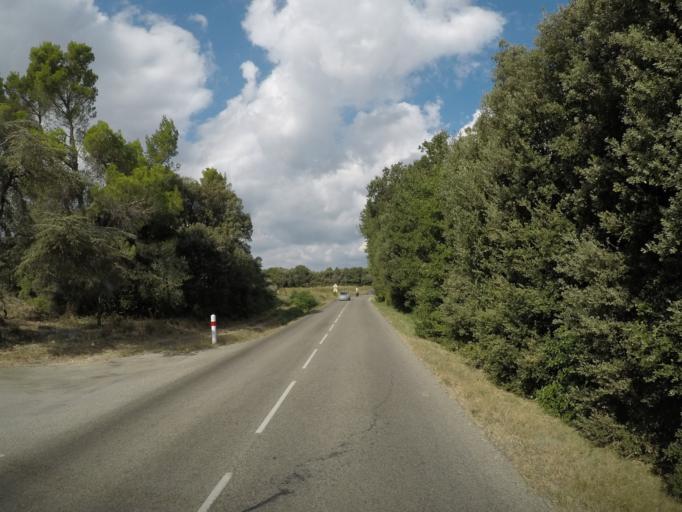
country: FR
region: Rhone-Alpes
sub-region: Departement de la Drome
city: Suze-la-Rousse
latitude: 44.3162
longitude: 4.8250
